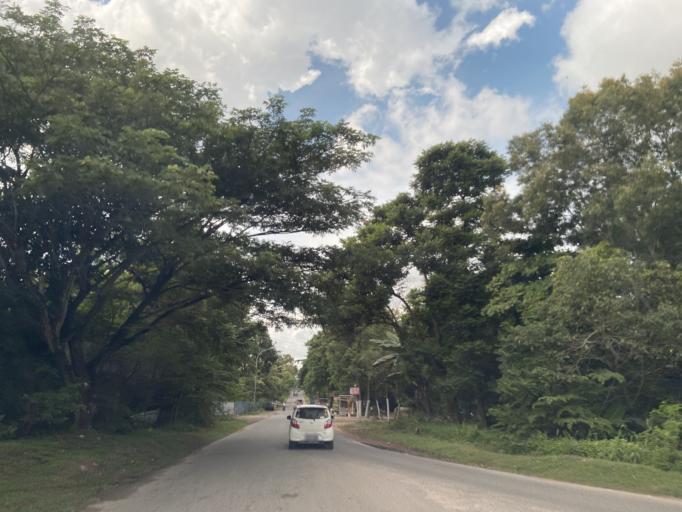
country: SG
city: Singapore
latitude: 1.1205
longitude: 104.0212
